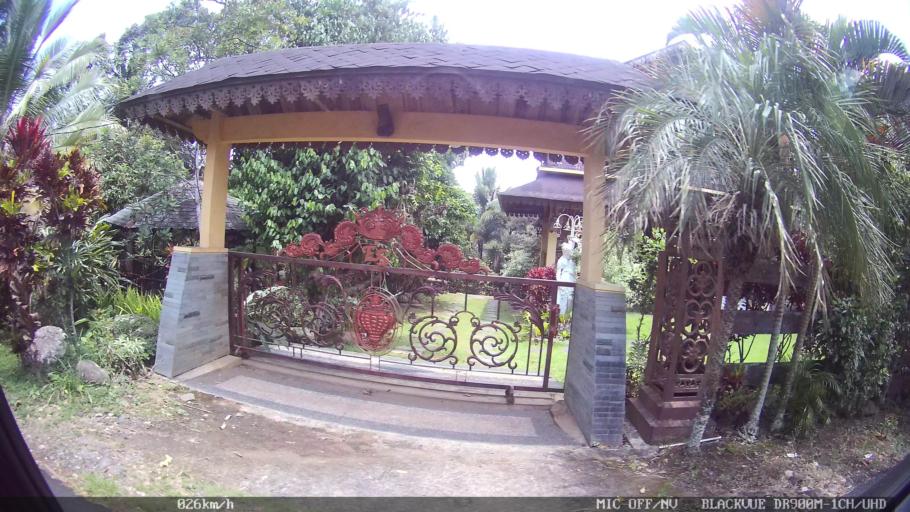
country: ID
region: Lampung
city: Bandarlampung
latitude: -5.4137
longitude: 105.2147
